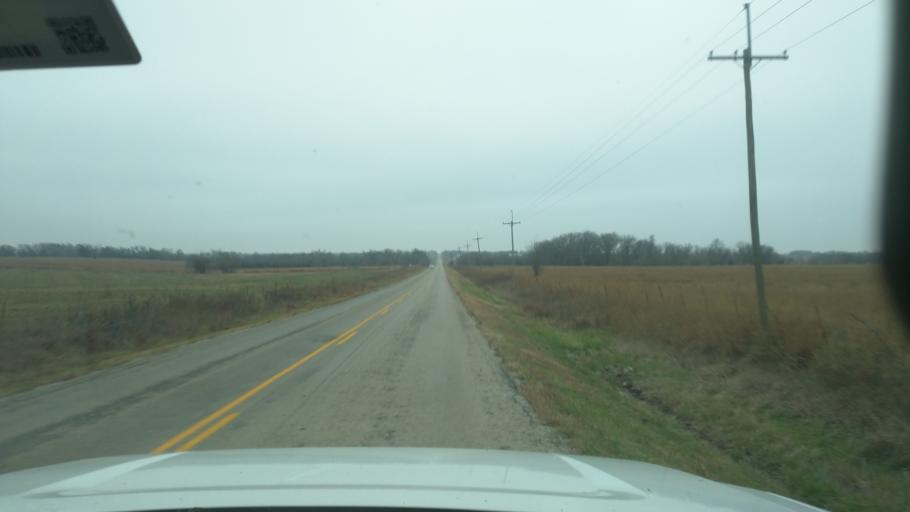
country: US
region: Kansas
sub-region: Lyon County
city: Emporia
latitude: 38.6009
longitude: -96.2609
